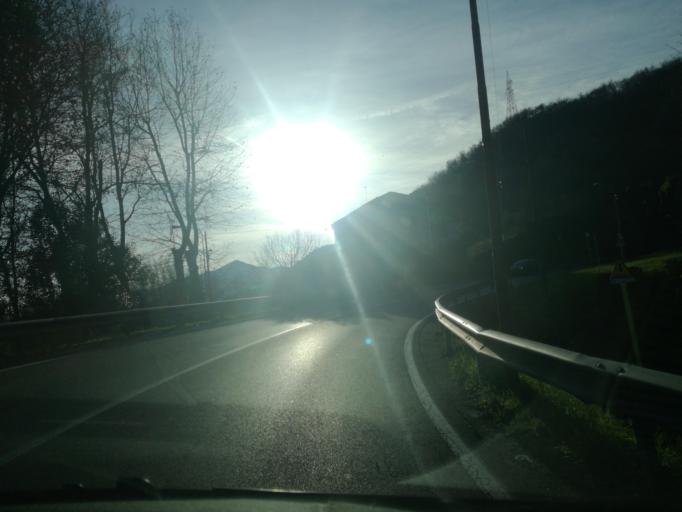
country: IT
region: Lombardy
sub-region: Provincia di Bergamo
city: Castro
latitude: 45.8072
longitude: 10.0644
